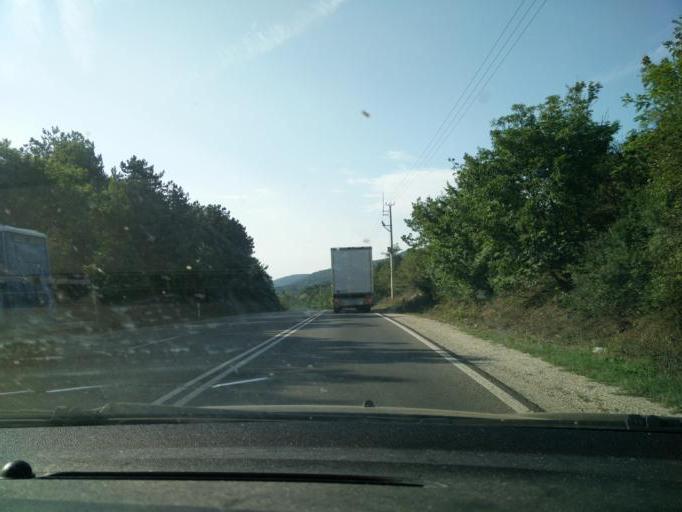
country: HU
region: Pest
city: Piliscsaba
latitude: 47.6251
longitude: 18.8611
